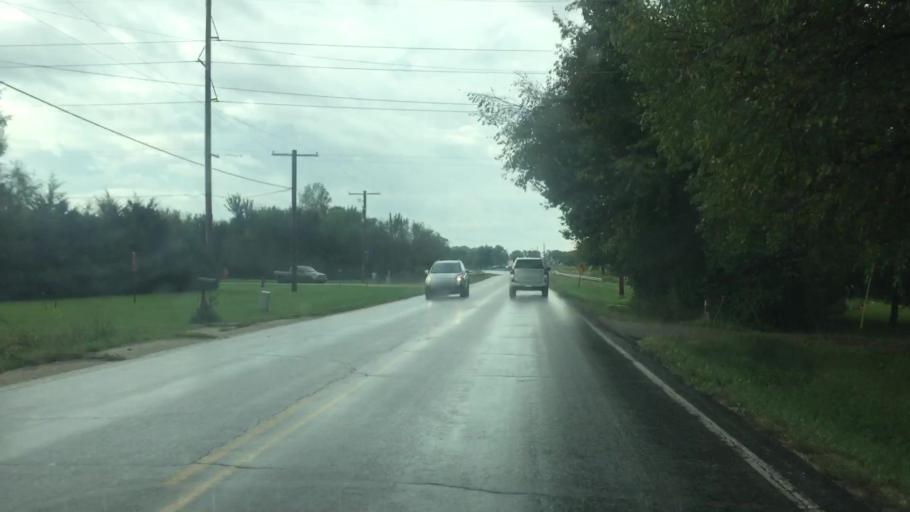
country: US
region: Kansas
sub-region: Allen County
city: Iola
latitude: 37.8936
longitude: -95.4095
